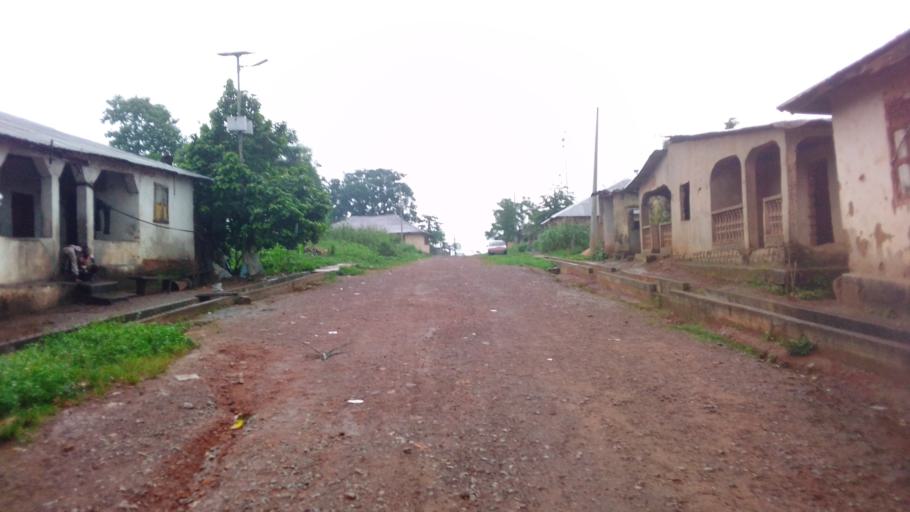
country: SL
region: Northern Province
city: Lunsar
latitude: 8.6826
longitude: -12.5302
